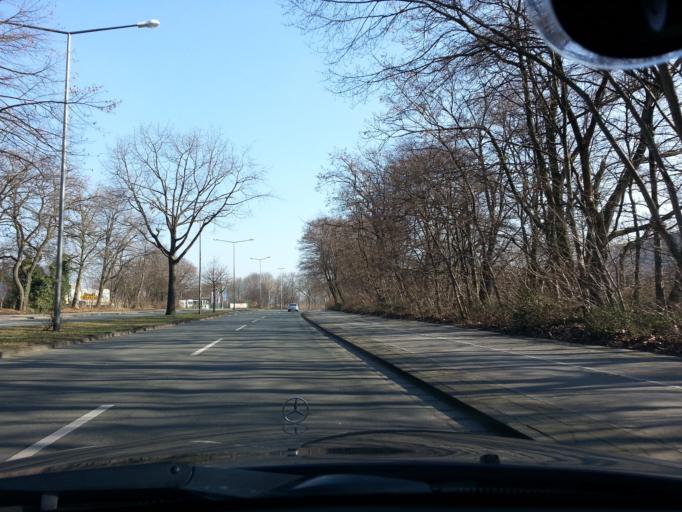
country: DE
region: North Rhine-Westphalia
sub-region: Regierungsbezirk Munster
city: Gelsenkirchen
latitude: 51.5520
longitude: 7.0868
